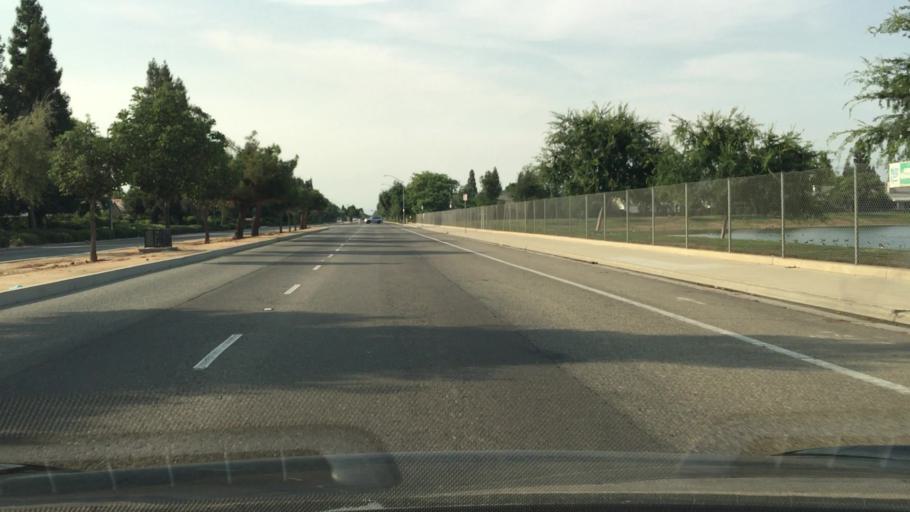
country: US
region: California
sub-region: Fresno County
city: Clovis
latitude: 36.8468
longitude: -119.7387
